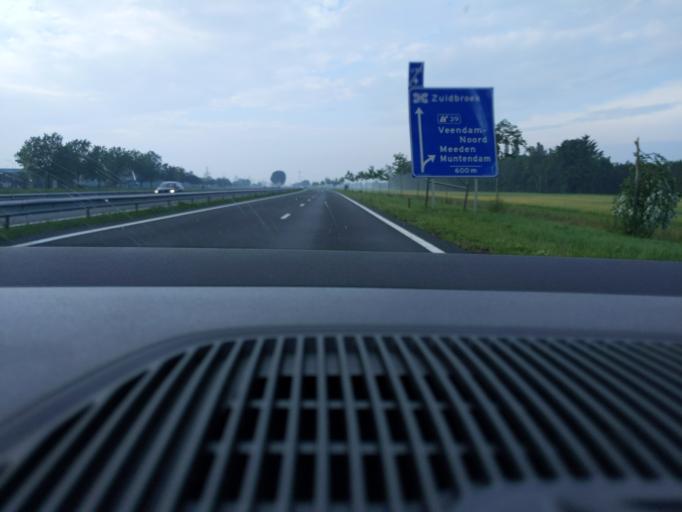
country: NL
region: Groningen
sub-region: Gemeente Veendam
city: Veendam
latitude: 53.1238
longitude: 6.8996
